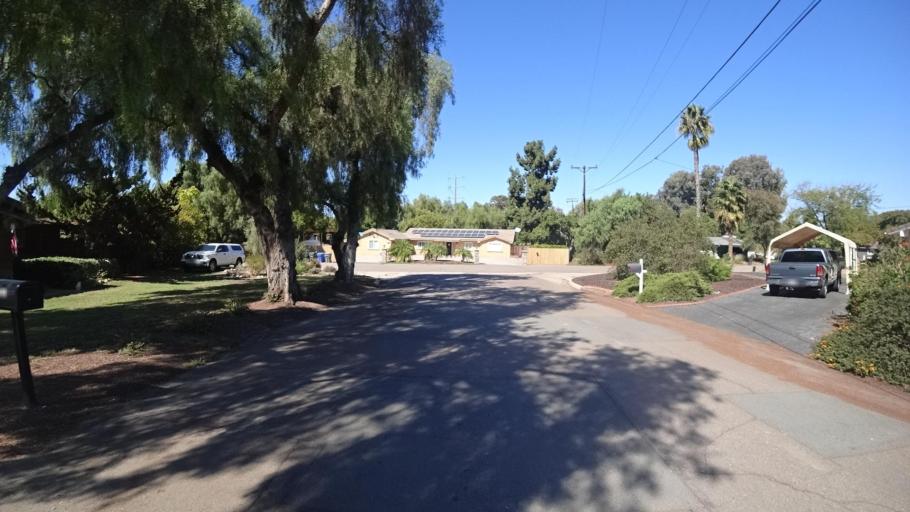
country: US
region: California
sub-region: San Diego County
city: Bonita
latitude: 32.6637
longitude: -117.0249
